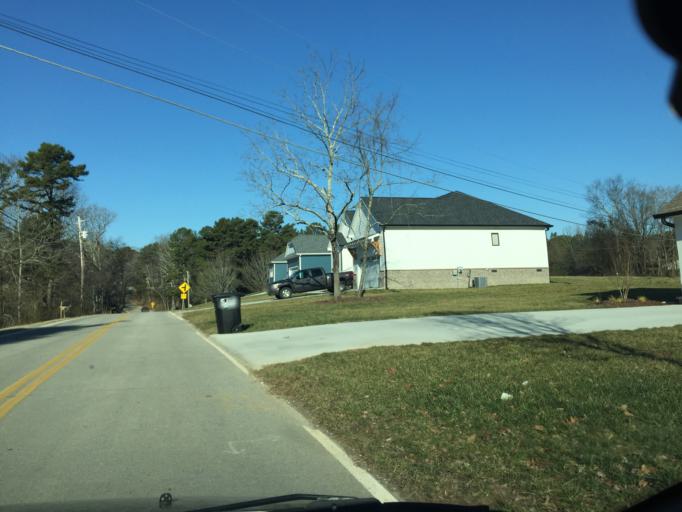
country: US
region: Tennessee
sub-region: Hamilton County
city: Collegedale
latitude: 35.0543
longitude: -85.1125
